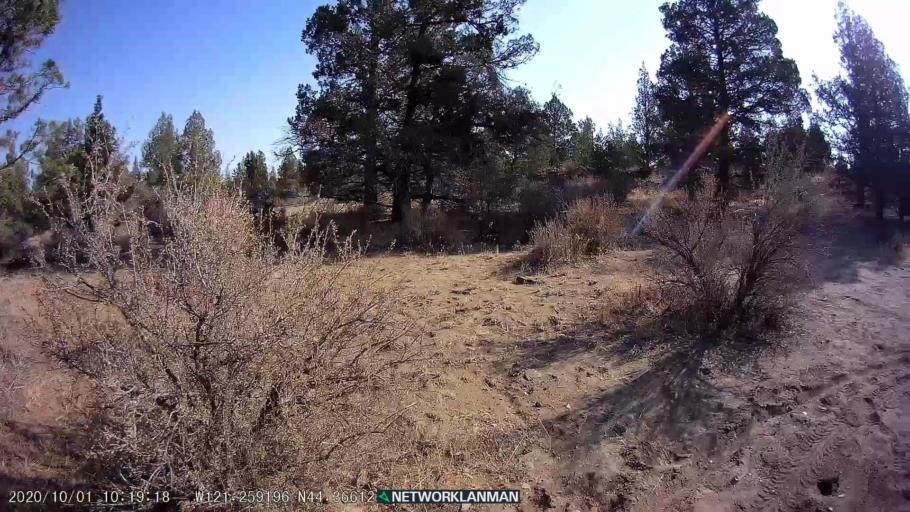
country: US
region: Oregon
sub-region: Deschutes County
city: Terrebonne
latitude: 44.3661
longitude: -121.2591
